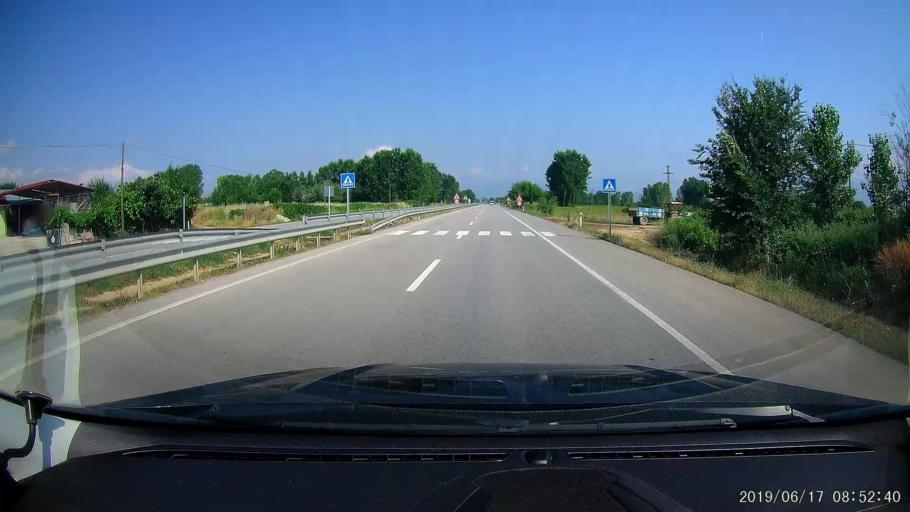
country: TR
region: Tokat
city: Erbaa
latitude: 40.7007
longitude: 36.4931
